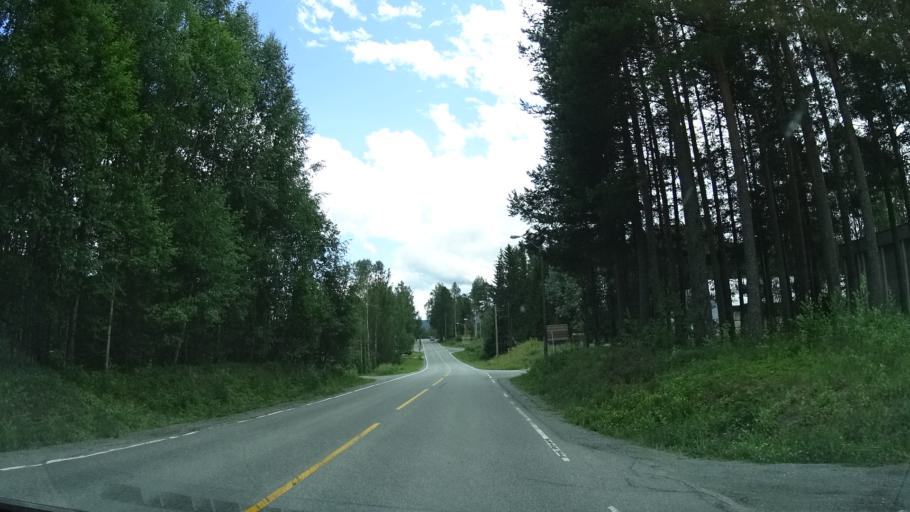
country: NO
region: Buskerud
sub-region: Krodsherad
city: Noresund
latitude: 60.1862
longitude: 9.6132
